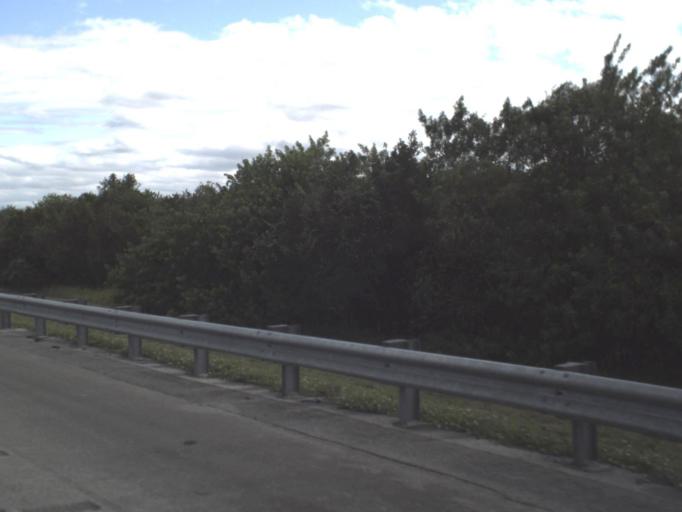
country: US
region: Florida
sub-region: Saint Lucie County
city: Lakewood Park
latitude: 27.4833
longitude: -80.4591
